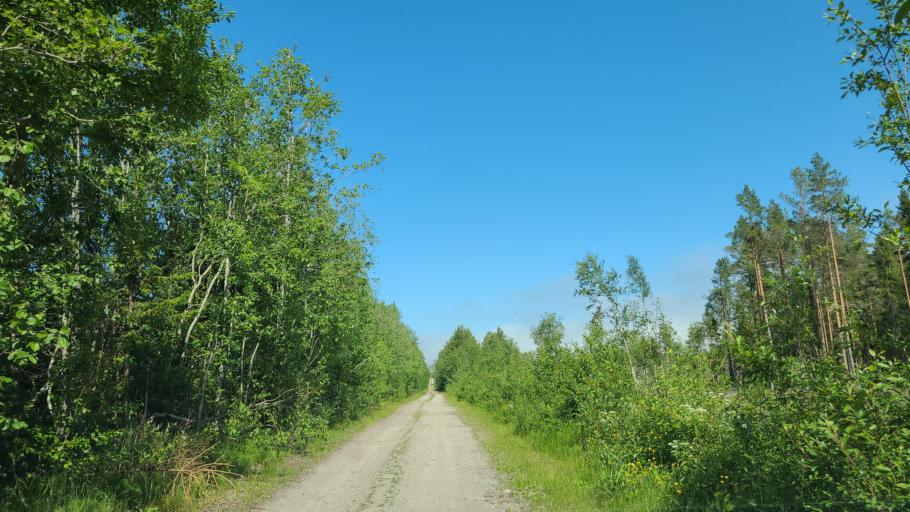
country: SE
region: Vaesternorrland
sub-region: OErnskoeldsviks Kommun
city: Husum
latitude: 63.4268
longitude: 19.2265
